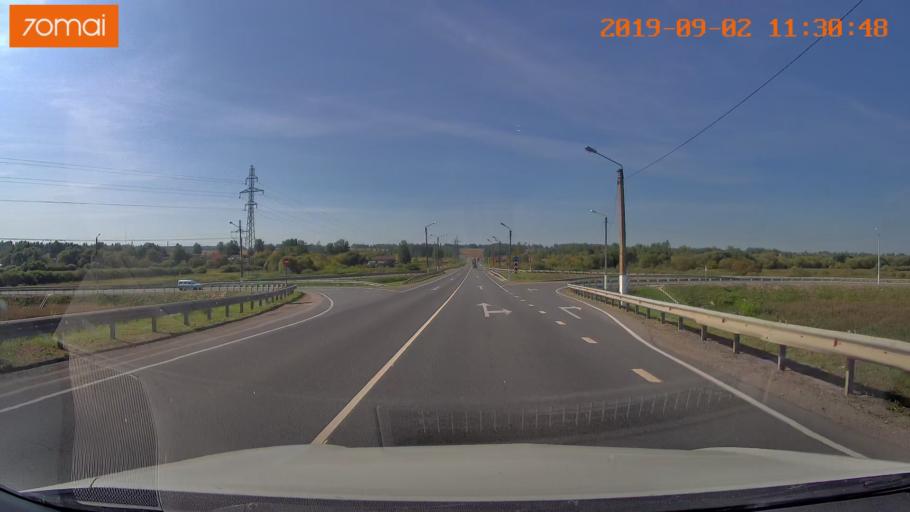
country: RU
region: Smolensk
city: Oster
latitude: 53.9806
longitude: 32.8263
